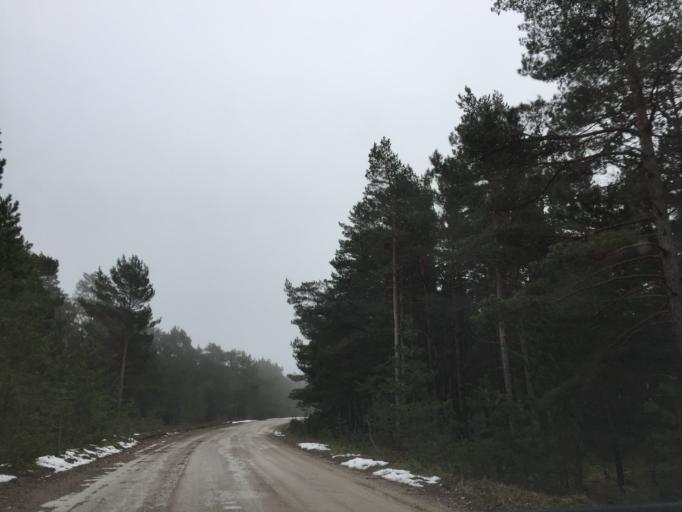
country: EE
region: Saare
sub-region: Kuressaare linn
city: Kuressaare
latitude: 58.4976
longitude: 21.9826
